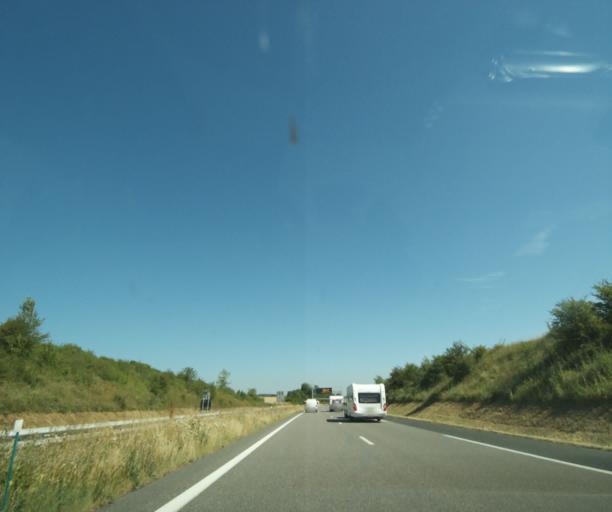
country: FR
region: Lorraine
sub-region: Departement des Vosges
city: Chatenois
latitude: 48.2764
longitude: 5.8568
